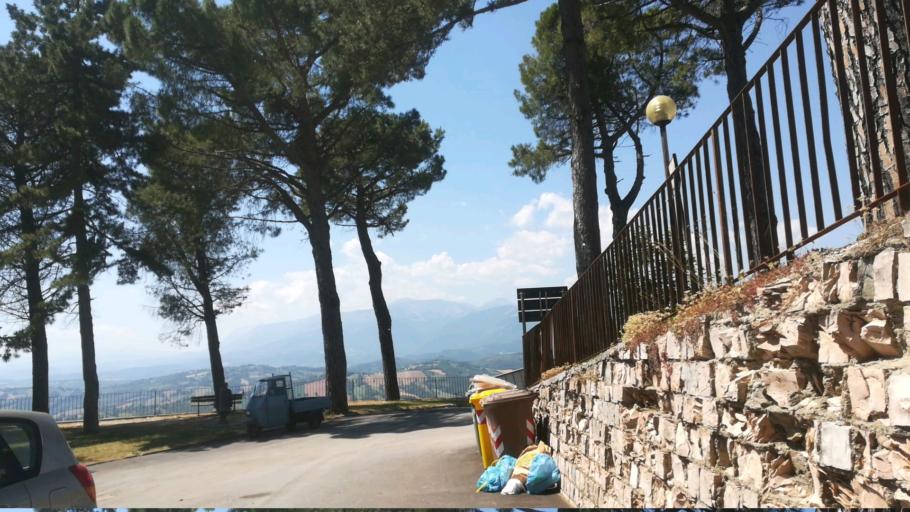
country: IT
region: The Marches
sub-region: Provincia di Macerata
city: San Ginesio
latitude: 43.1064
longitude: 13.3162
